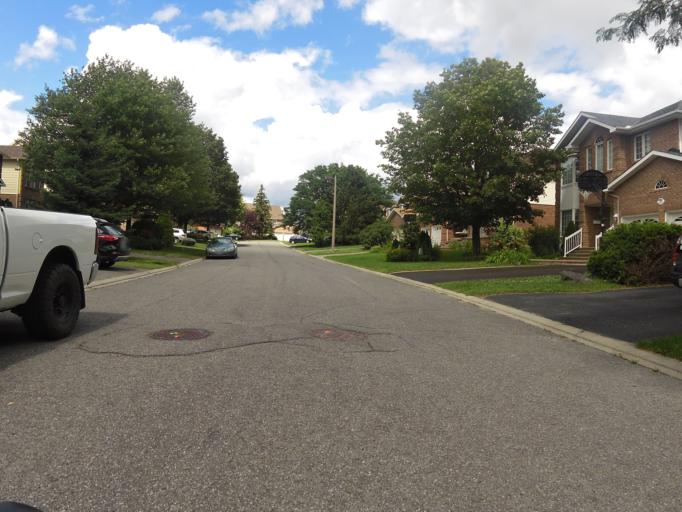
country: CA
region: Ontario
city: Bells Corners
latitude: 45.3189
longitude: -75.9100
